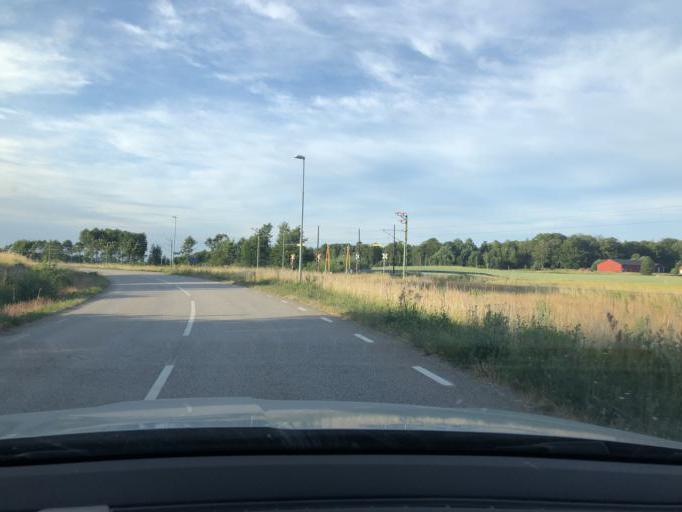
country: SE
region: Blekinge
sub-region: Solvesborgs Kommun
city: Soelvesborg
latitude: 56.0740
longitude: 14.6116
